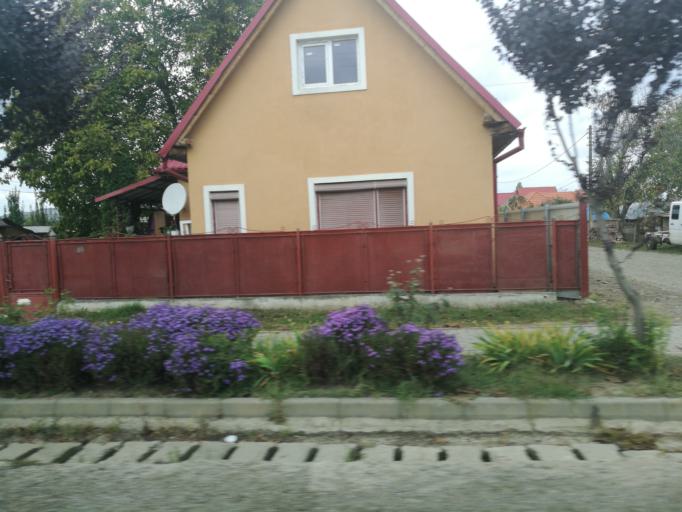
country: RO
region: Mures
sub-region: Comuna Ungheni
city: Ungheni
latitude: 46.4905
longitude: 24.4675
